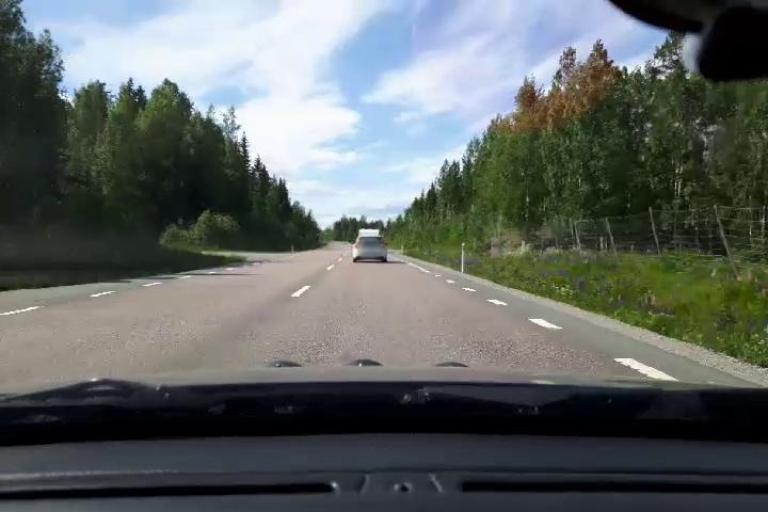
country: SE
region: Gaevleborg
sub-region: Bollnas Kommun
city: Kilafors
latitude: 61.2859
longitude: 16.5143
